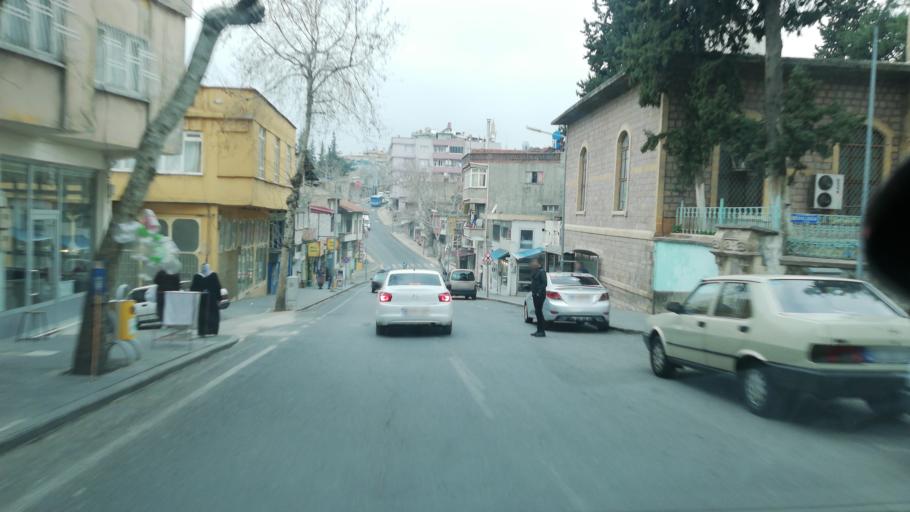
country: TR
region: Kahramanmaras
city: Kahramanmaras
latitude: 37.5900
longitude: 36.9280
